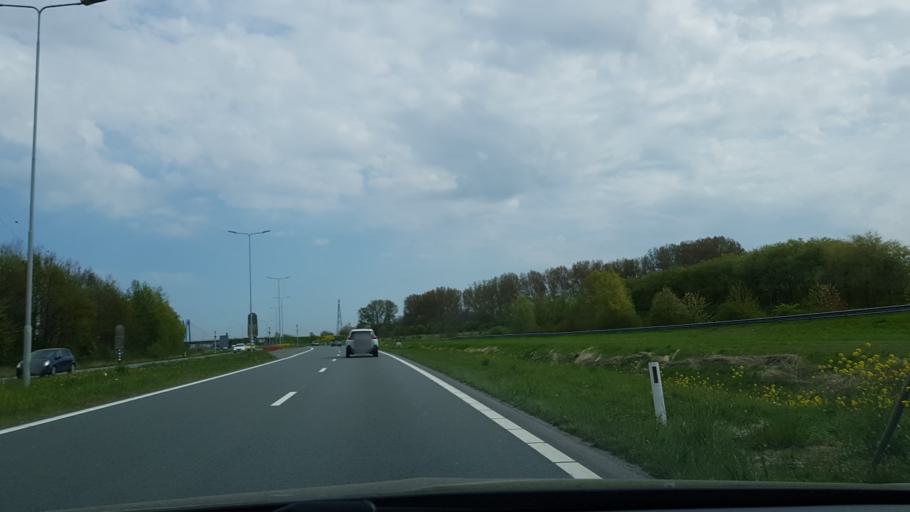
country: NL
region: North Holland
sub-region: Gemeente Haarlemmermeer
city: Hoofddorp
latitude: 52.3313
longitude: 4.6655
